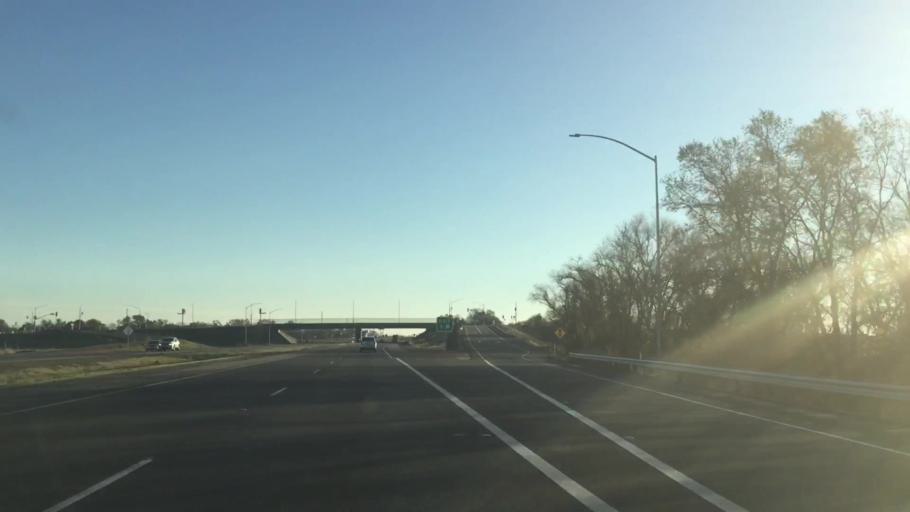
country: US
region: California
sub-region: Yuba County
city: Plumas Lake
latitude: 38.9818
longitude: -121.5433
